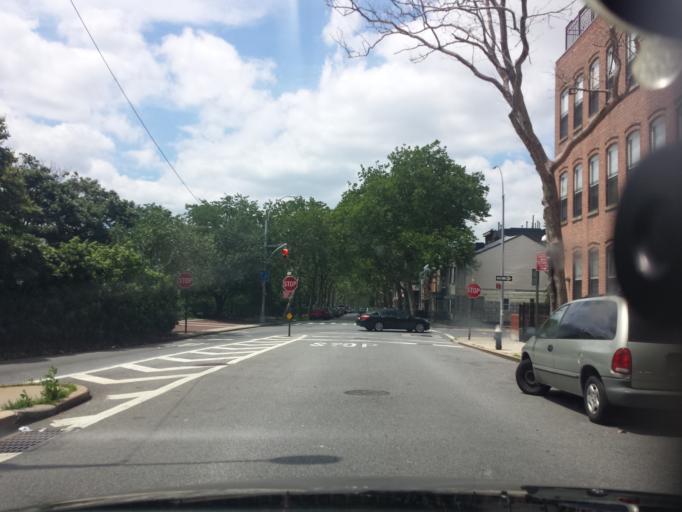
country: US
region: New York
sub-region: Kings County
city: Brooklyn
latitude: 40.6589
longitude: -73.9847
